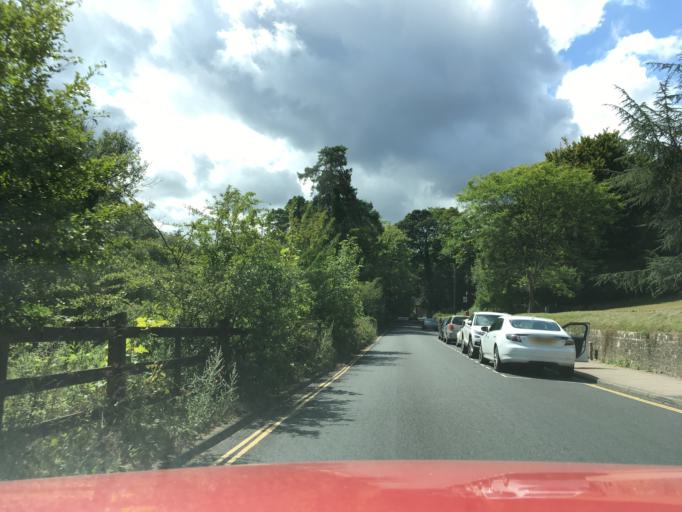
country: GB
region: England
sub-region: Kent
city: West Malling
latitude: 51.2900
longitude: 0.4055
